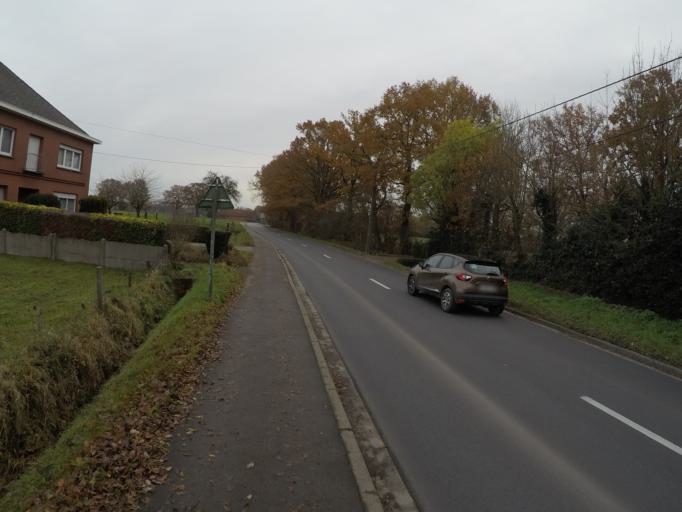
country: BE
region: Flanders
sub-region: Provincie Antwerpen
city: Berlaar
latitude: 51.1098
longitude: 4.6732
